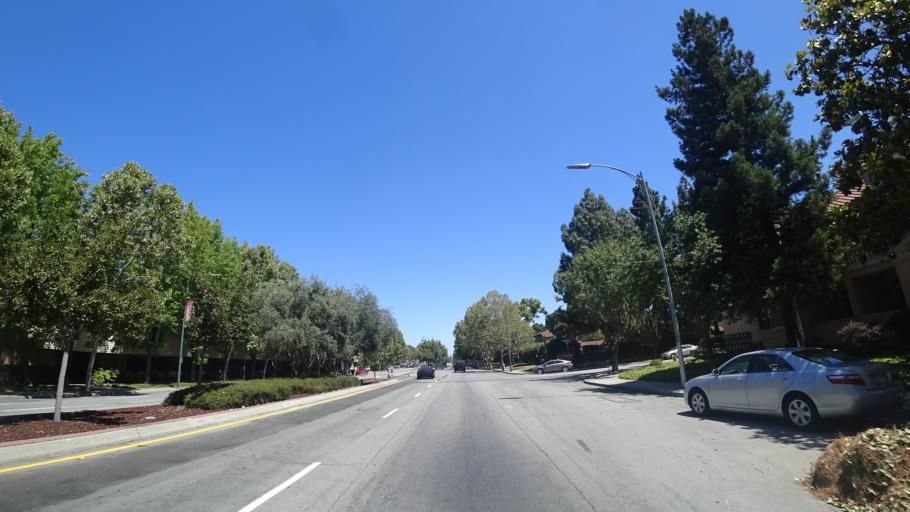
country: US
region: California
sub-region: Santa Clara County
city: Campbell
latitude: 37.3060
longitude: -121.9500
